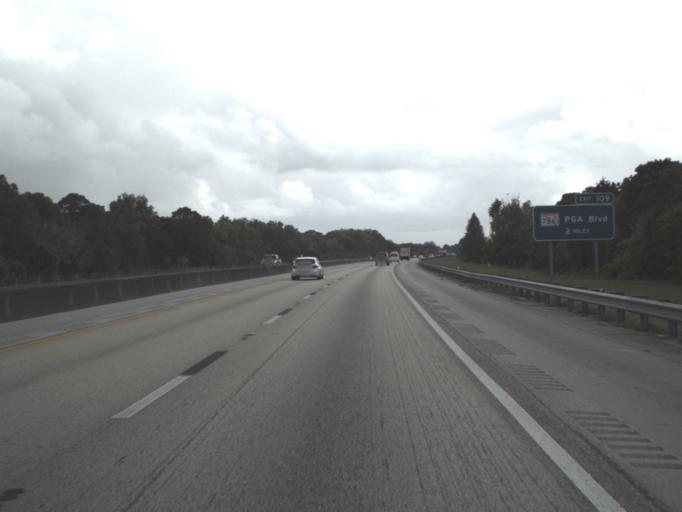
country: US
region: Florida
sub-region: Palm Beach County
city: Palm Beach Gardens
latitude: 26.8757
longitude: -80.1292
